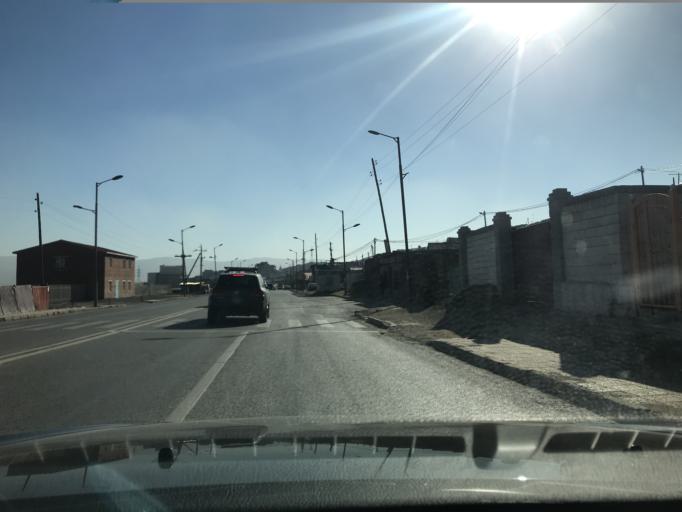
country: MN
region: Ulaanbaatar
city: Ulaanbaatar
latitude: 47.9746
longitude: 106.9181
